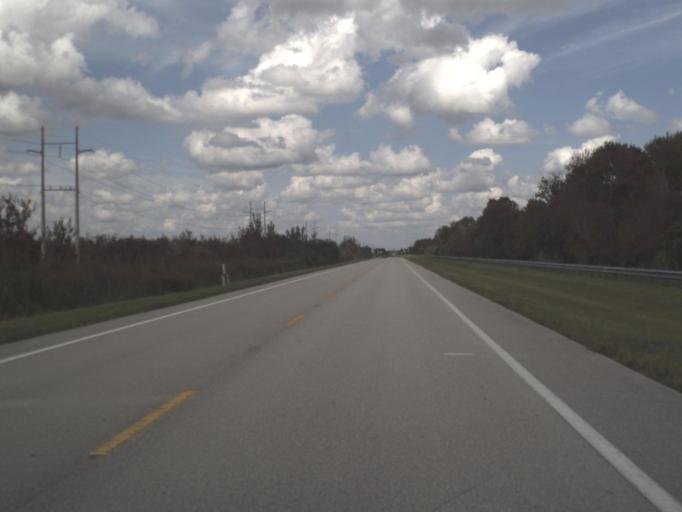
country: US
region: Florida
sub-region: Collier County
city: Lely Resort
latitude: 25.9598
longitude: -81.3549
